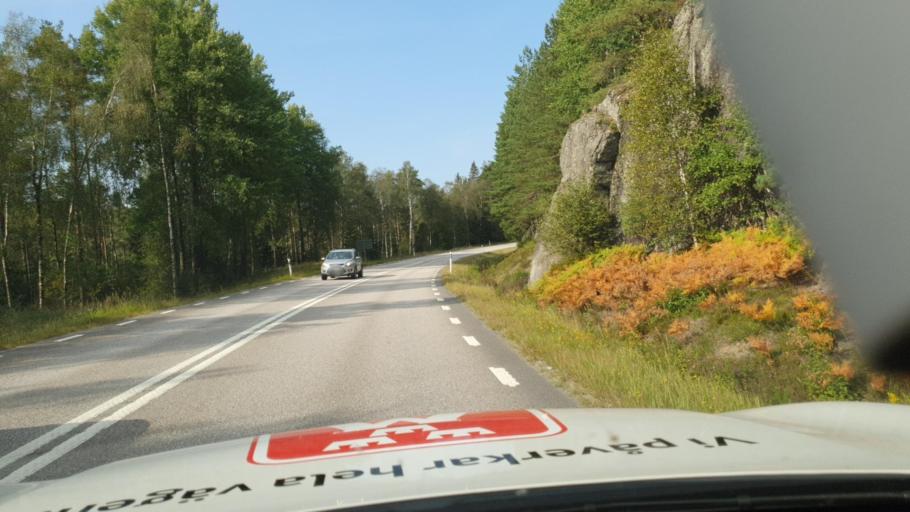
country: SE
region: Vaestra Goetaland
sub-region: Dals-Ed Kommun
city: Ed
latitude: 58.8799
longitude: 11.8196
